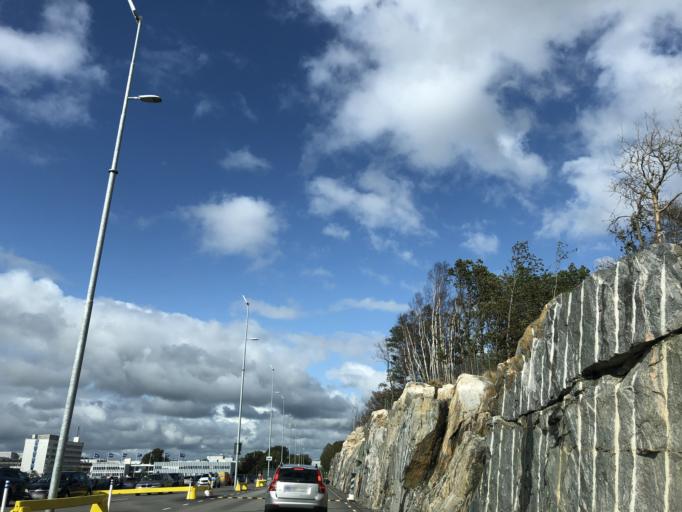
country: SE
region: Vaestra Goetaland
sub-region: Goteborg
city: Torslanda
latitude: 57.7159
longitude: 11.8432
